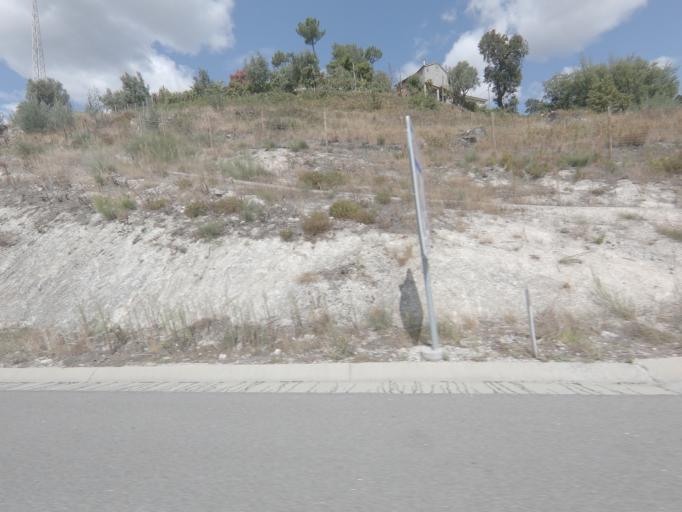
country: PT
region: Porto
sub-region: Baiao
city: Valadares
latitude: 41.2518
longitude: -7.9686
